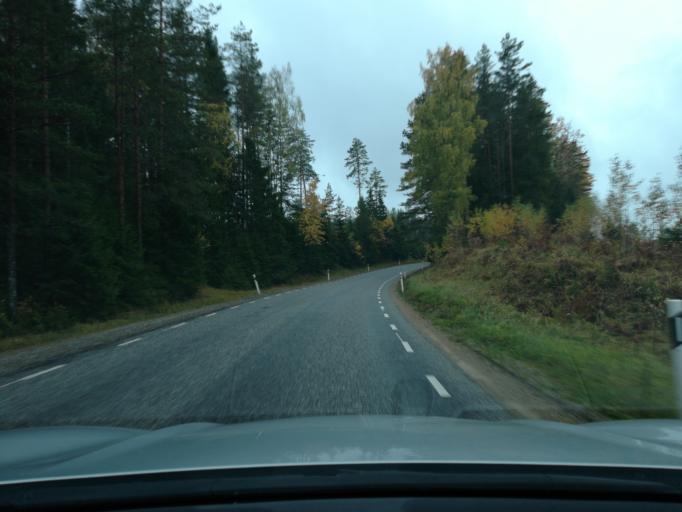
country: EE
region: Ida-Virumaa
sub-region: Johvi vald
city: Johvi
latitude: 59.1758
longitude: 27.4567
